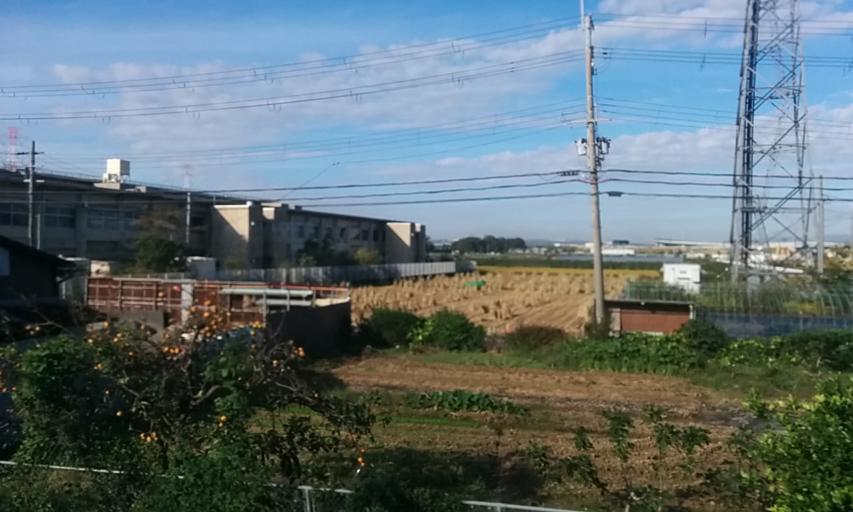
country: JP
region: Kyoto
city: Tanabe
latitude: 34.8457
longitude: 135.7723
